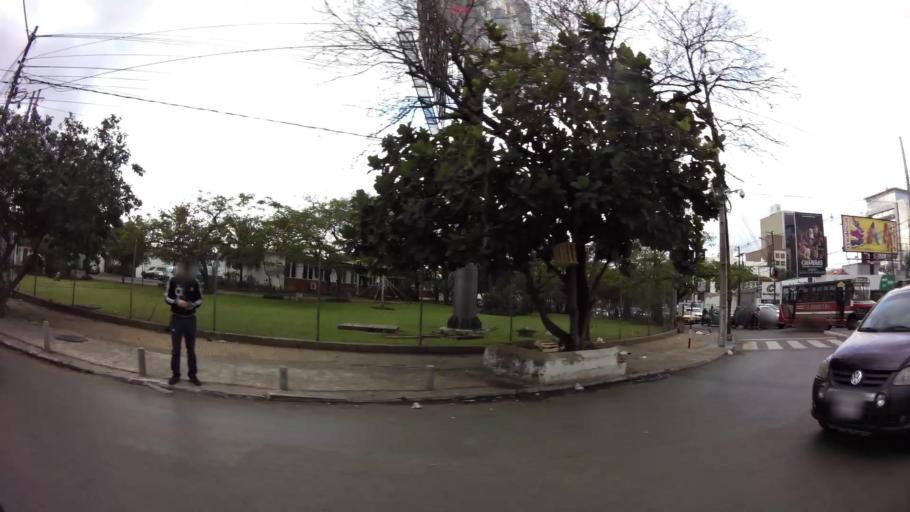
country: PY
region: Asuncion
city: Asuncion
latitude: -25.2864
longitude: -57.5721
